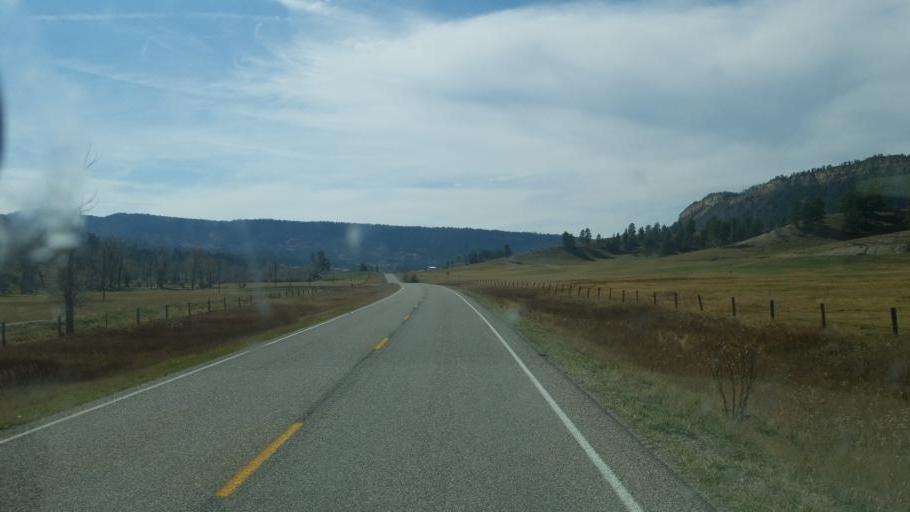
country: US
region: New Mexico
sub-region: Rio Arriba County
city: Dulce
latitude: 37.0580
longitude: -106.8380
